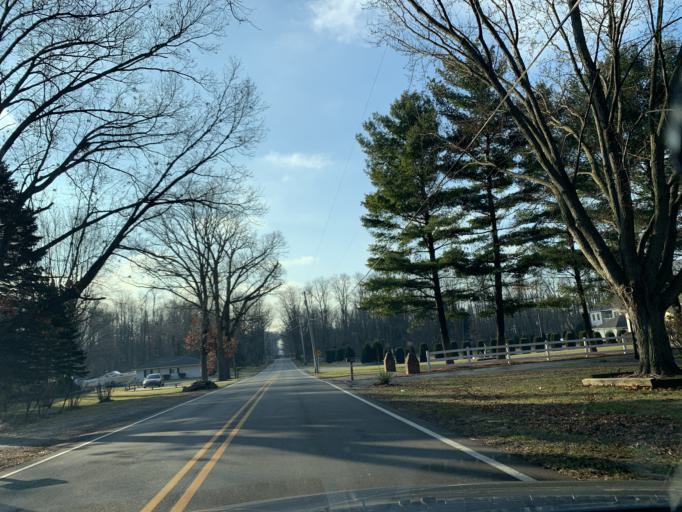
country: US
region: Indiana
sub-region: Porter County
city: Portage
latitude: 41.5855
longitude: -87.1536
